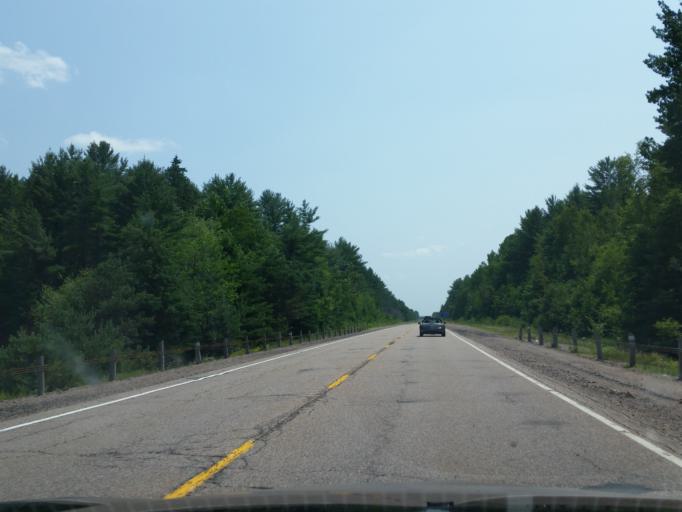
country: CA
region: Ontario
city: Petawawa
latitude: 45.8427
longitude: -77.2626
